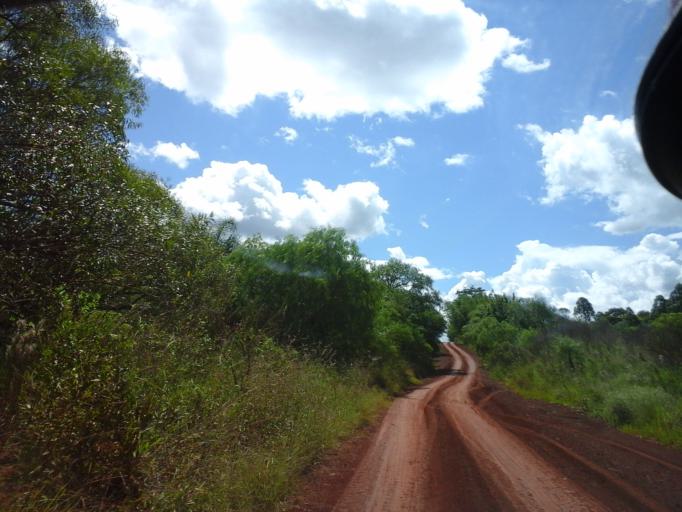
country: AR
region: Misiones
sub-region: Departamento de Apostoles
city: Apostoles
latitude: -27.9749
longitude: -55.7739
